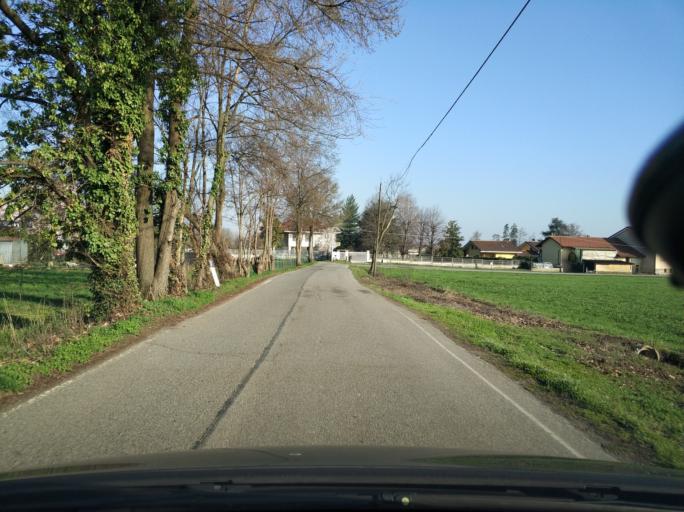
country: IT
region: Piedmont
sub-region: Provincia di Torino
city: Cirie
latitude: 45.2012
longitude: 7.6041
